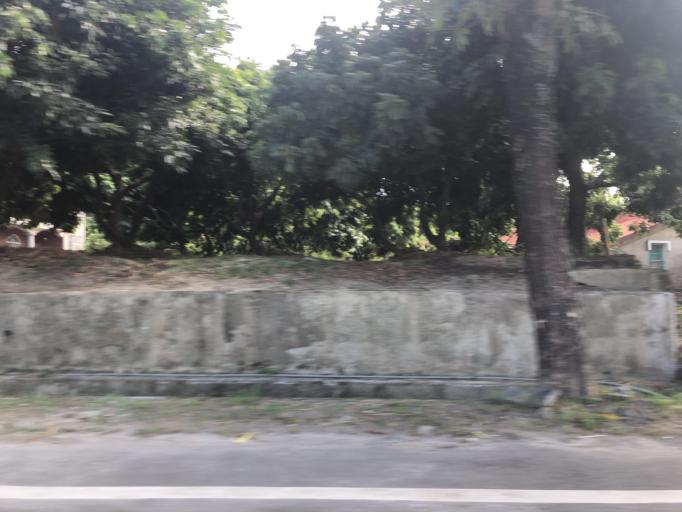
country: TW
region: Taiwan
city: Yujing
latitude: 23.0535
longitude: 120.4134
